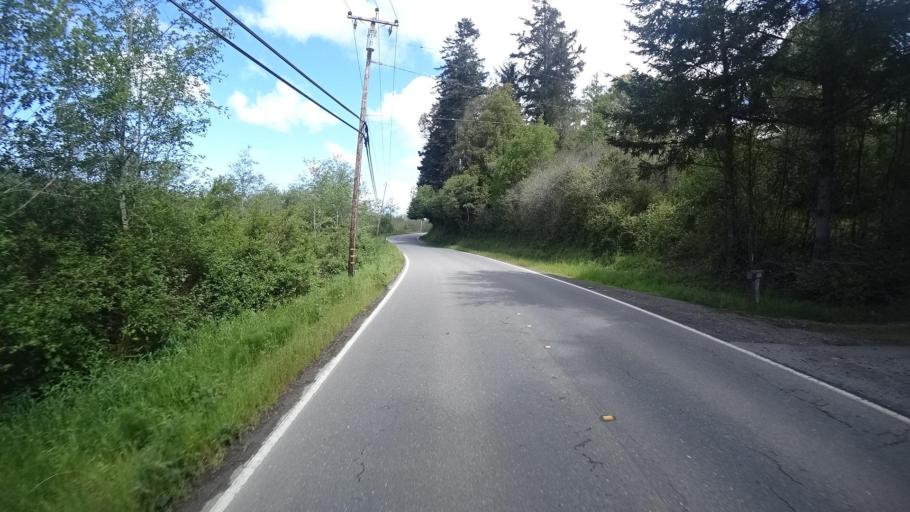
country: US
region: California
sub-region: Humboldt County
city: Blue Lake
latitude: 40.9048
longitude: -124.0251
